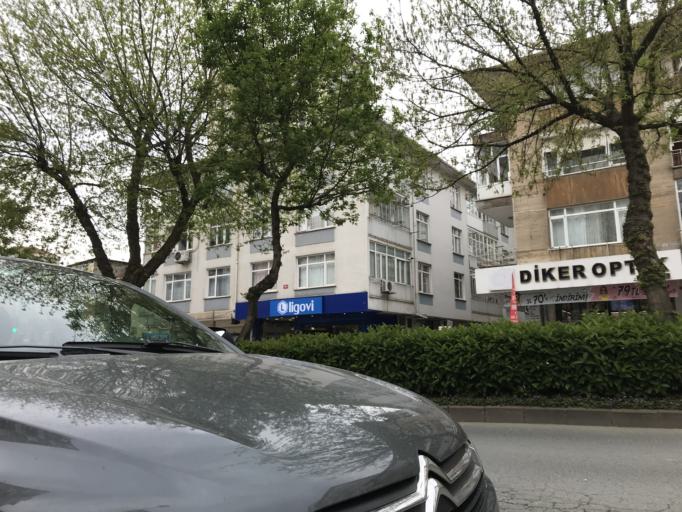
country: TR
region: Istanbul
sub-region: Atasehir
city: Atasehir
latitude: 40.9801
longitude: 29.0674
